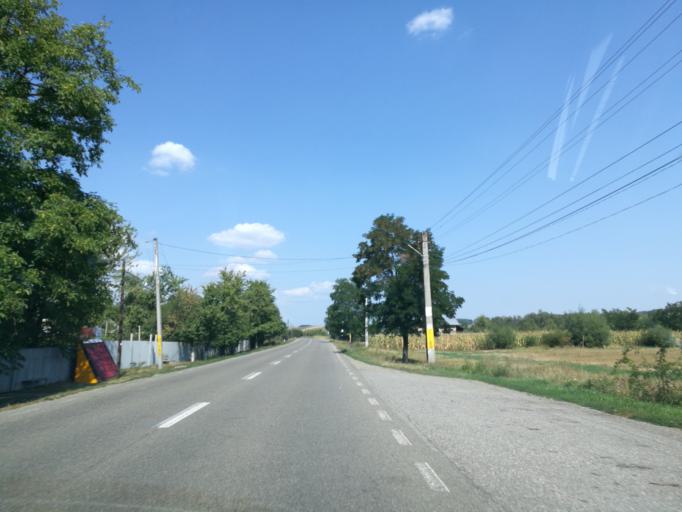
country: RO
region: Neamt
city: Bodesti
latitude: 47.0443
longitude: 26.4056
